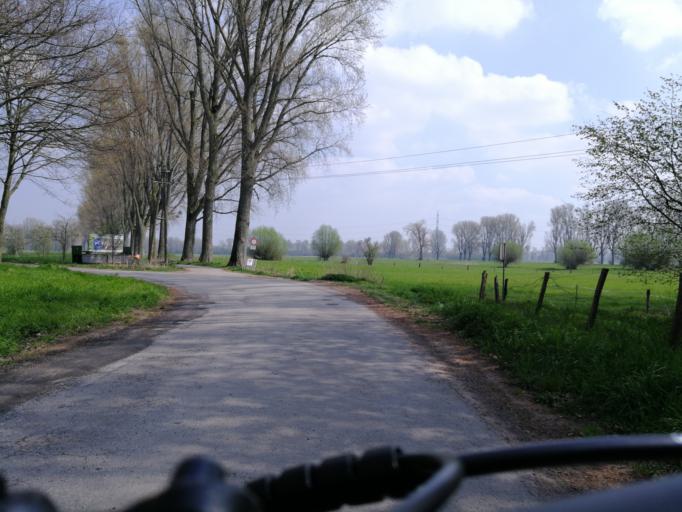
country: DE
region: North Rhine-Westphalia
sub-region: Regierungsbezirk Dusseldorf
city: Dormagen
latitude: 51.1438
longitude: 6.8254
